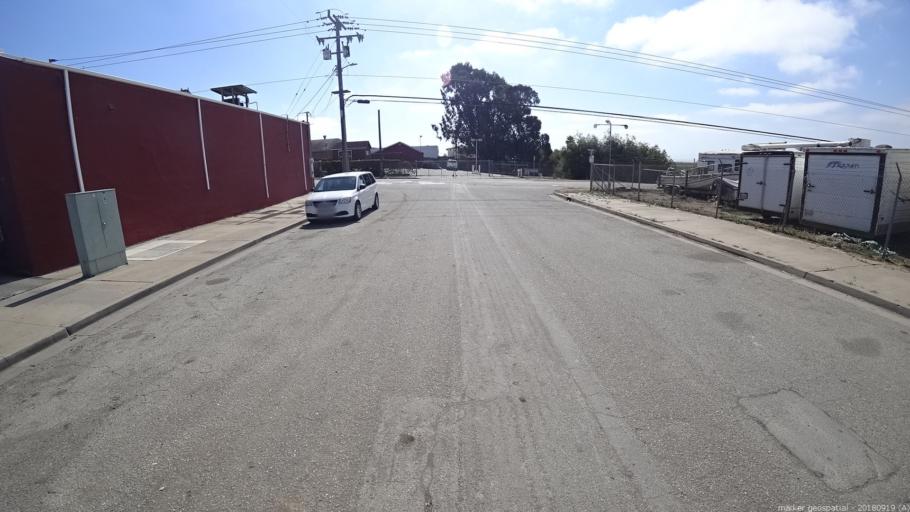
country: US
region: California
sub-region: Monterey County
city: Castroville
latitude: 36.7658
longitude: -121.7591
